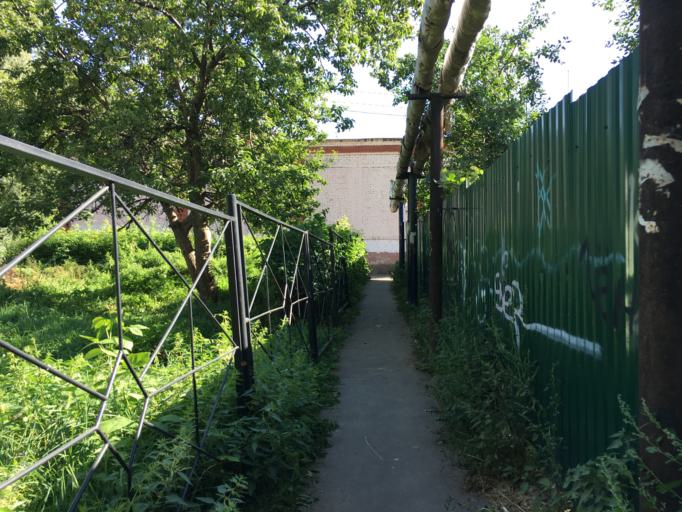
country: RU
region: Mariy-El
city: Yoshkar-Ola
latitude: 56.6442
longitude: 47.8671
